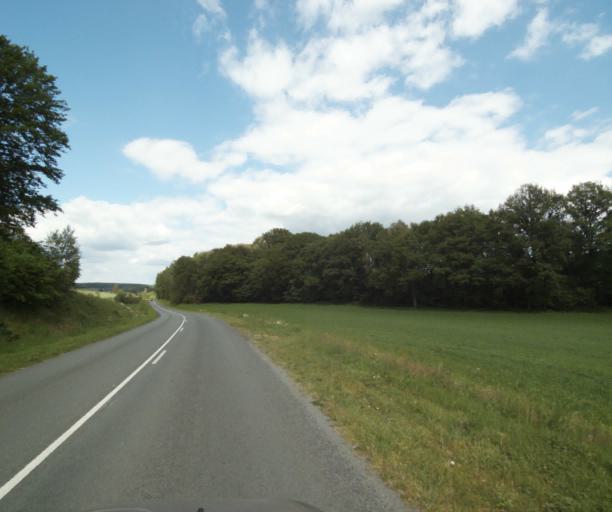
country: FR
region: Champagne-Ardenne
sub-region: Departement des Ardennes
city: Saint-Laurent
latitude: 49.7690
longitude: 4.7825
